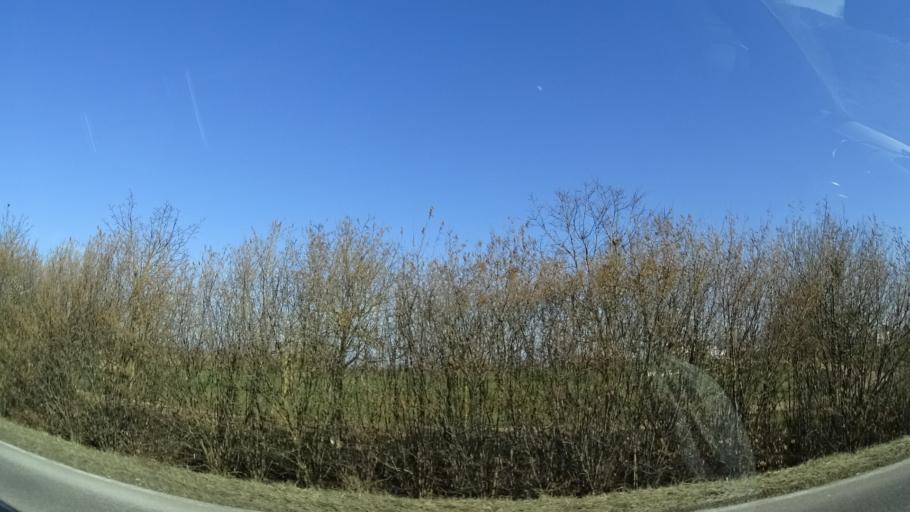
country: DE
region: Rheinland-Pfalz
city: Dackenheim
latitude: 49.5252
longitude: 8.1775
